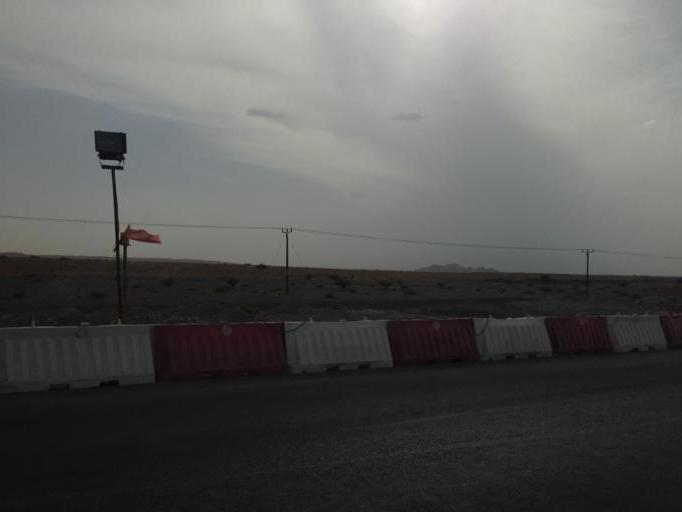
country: OM
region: Ash Sharqiyah
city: Al Qabil
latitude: 22.5372
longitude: 58.7297
